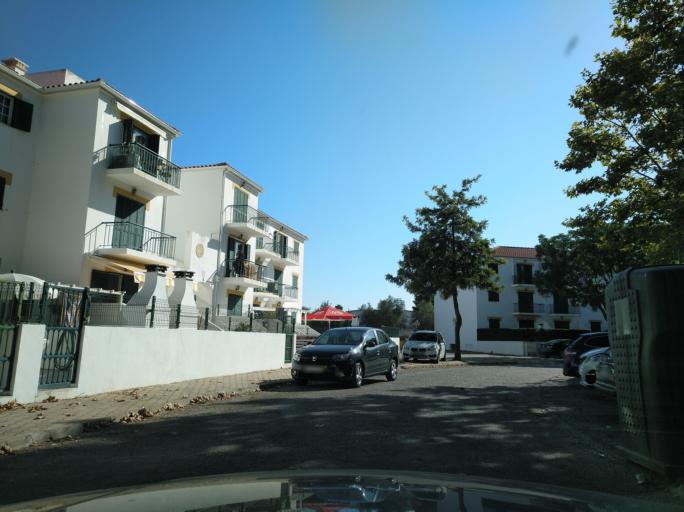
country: PT
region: Faro
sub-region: Vila Real de Santo Antonio
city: Monte Gordo
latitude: 37.1742
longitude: -7.5074
